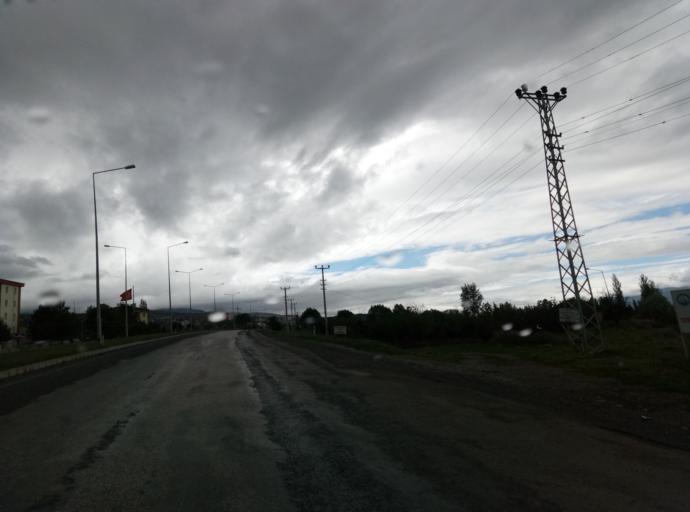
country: TR
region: Sivas
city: Susehri
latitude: 40.1690
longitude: 38.0985
